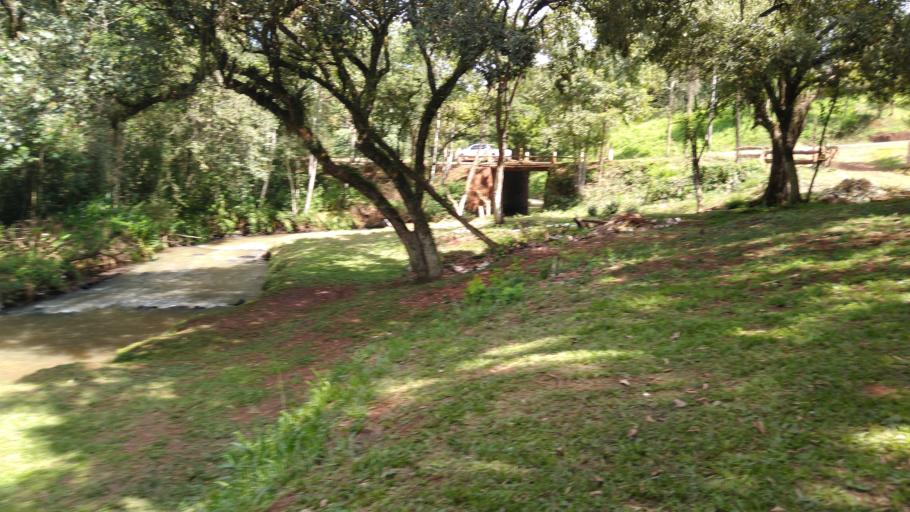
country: AR
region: Misiones
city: Puerto Libertad
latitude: -25.9676
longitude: -54.5829
